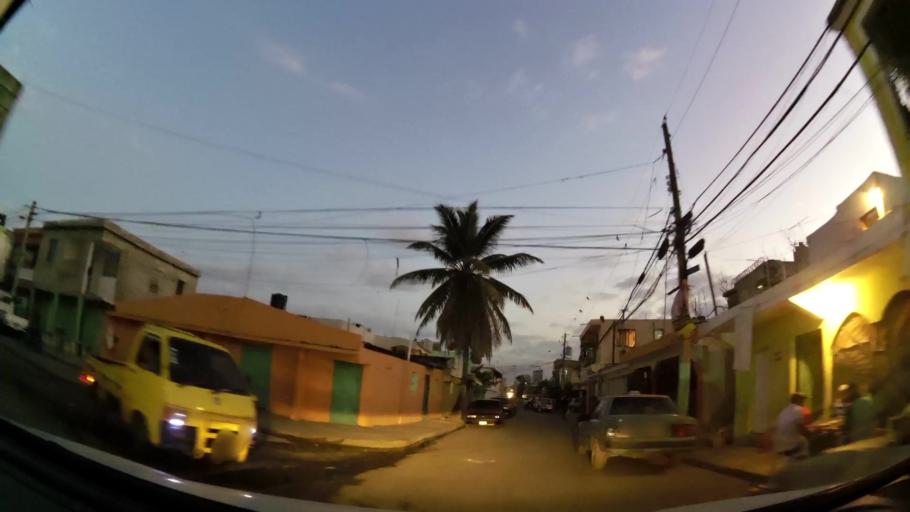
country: DO
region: Nacional
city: La Agustina
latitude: 18.5413
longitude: -69.9400
